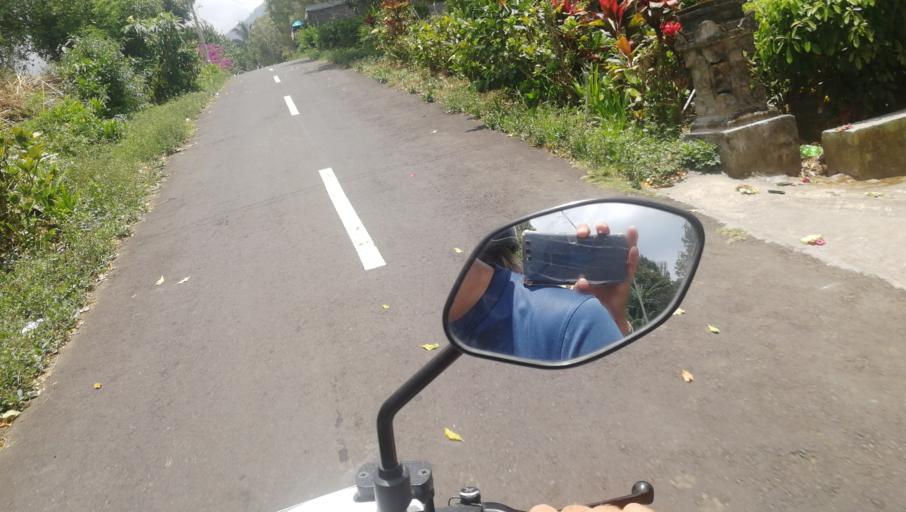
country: ID
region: Bali
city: Munduk
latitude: -8.2996
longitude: 115.0548
